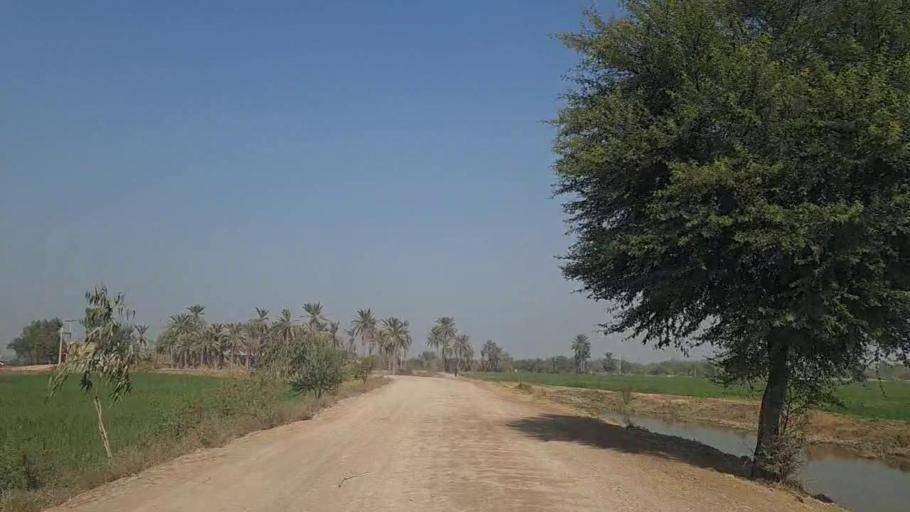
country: PK
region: Sindh
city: Nawabshah
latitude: 26.2338
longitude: 68.4940
